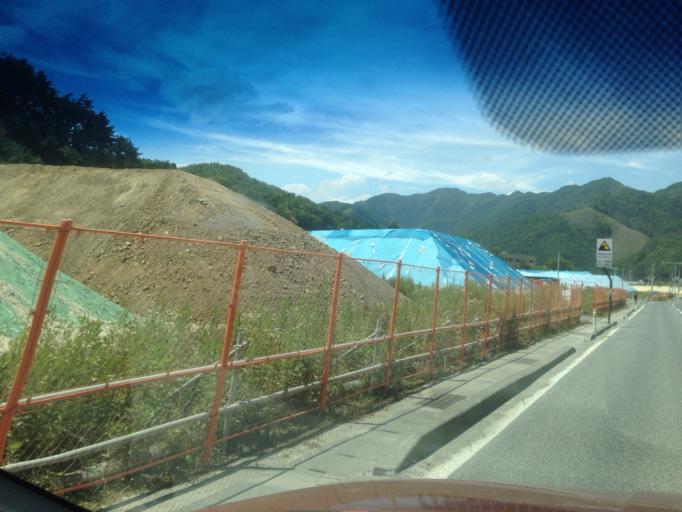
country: JP
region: Iwate
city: Otsuchi
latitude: 39.3283
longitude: 141.8853
